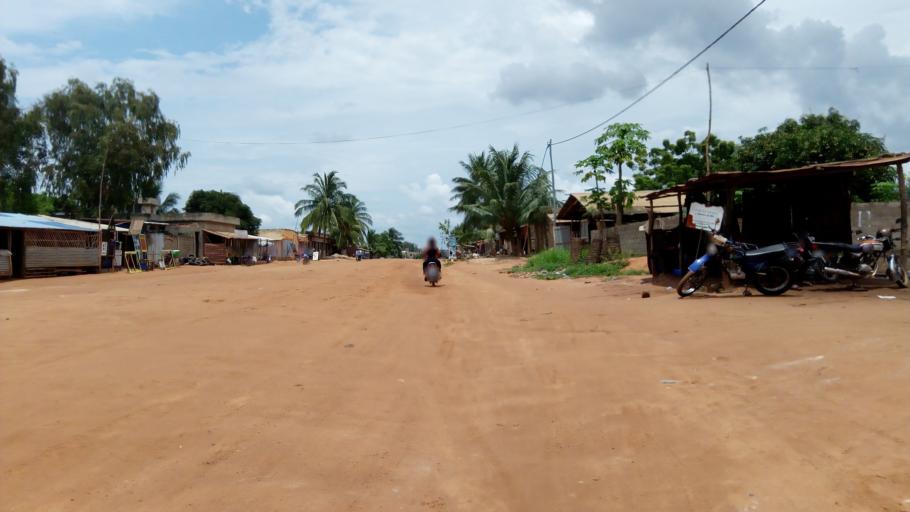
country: TG
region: Maritime
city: Lome
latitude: 6.2267
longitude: 1.1596
